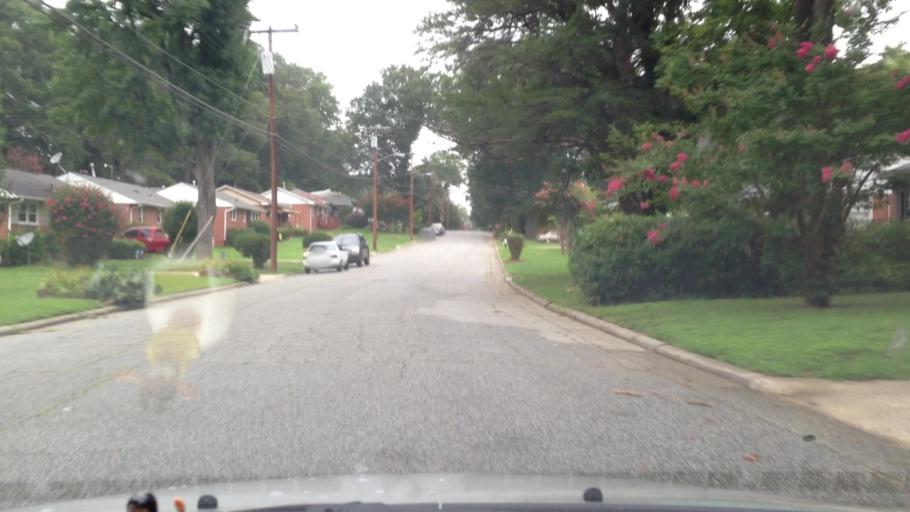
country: US
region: North Carolina
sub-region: Guilford County
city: Greensboro
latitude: 36.0519
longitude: -79.7635
